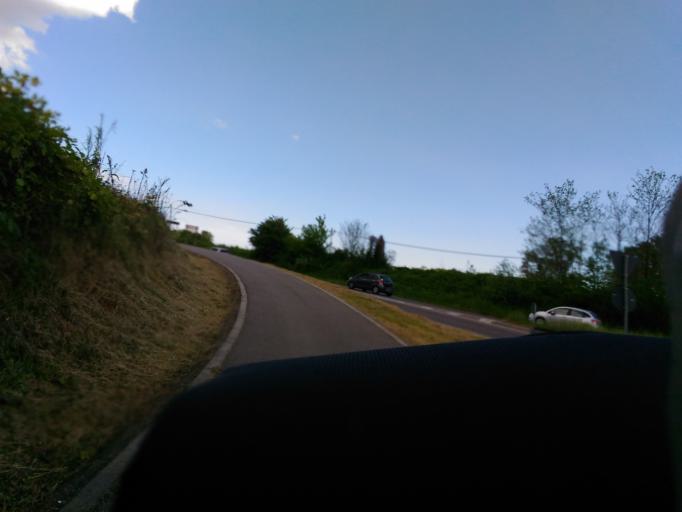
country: IT
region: Lombardy
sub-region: Citta metropolitana di Milano
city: Colturano
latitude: 45.3809
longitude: 9.3415
